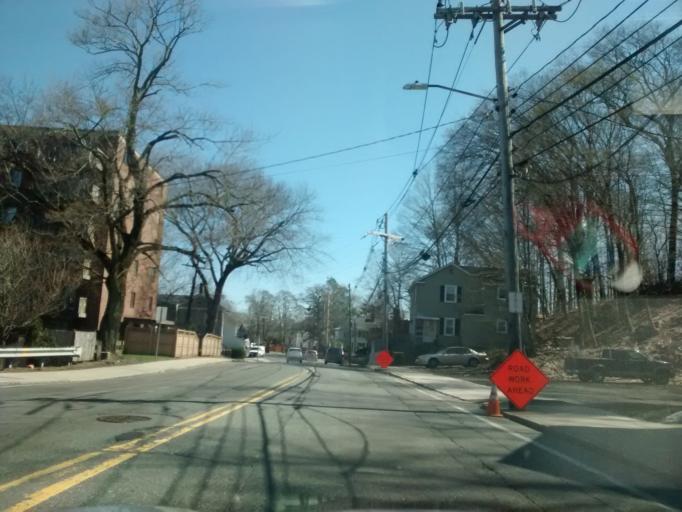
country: US
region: Massachusetts
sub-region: Middlesex County
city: Framingham Center
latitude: 42.2995
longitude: -71.4344
